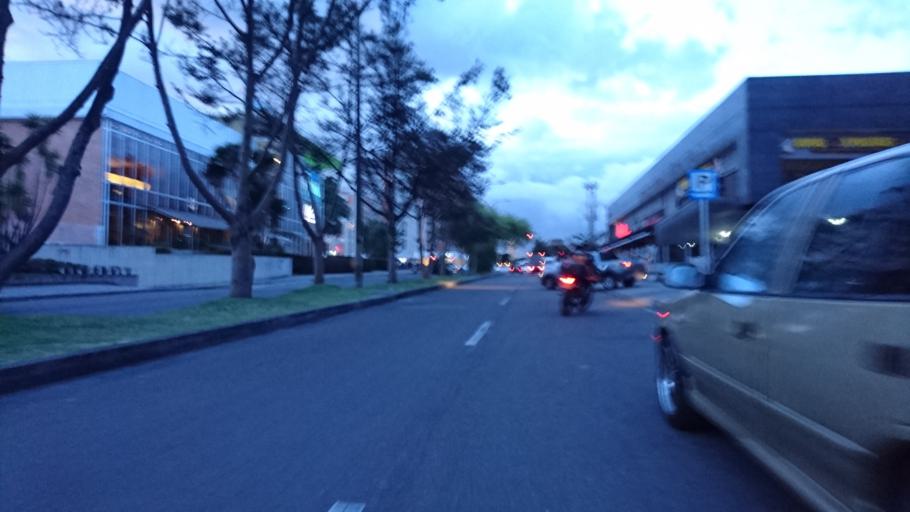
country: CO
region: Bogota D.C.
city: Barrio San Luis
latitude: 4.6872
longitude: -74.0733
